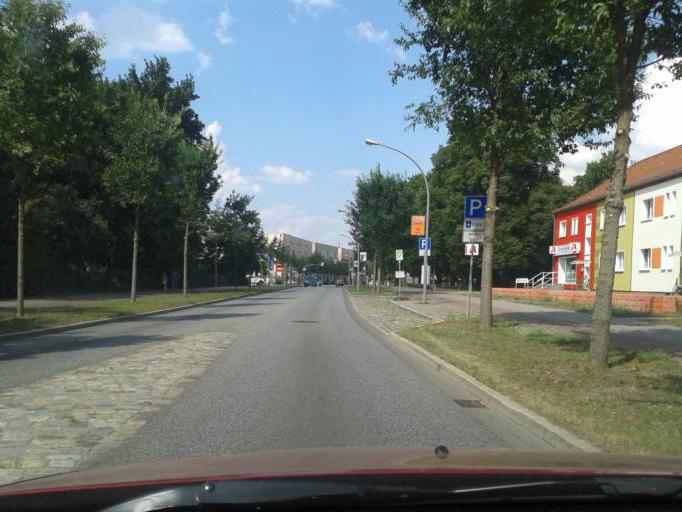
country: DE
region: Brandenburg
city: Oranienburg
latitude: 52.7432
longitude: 13.2386
